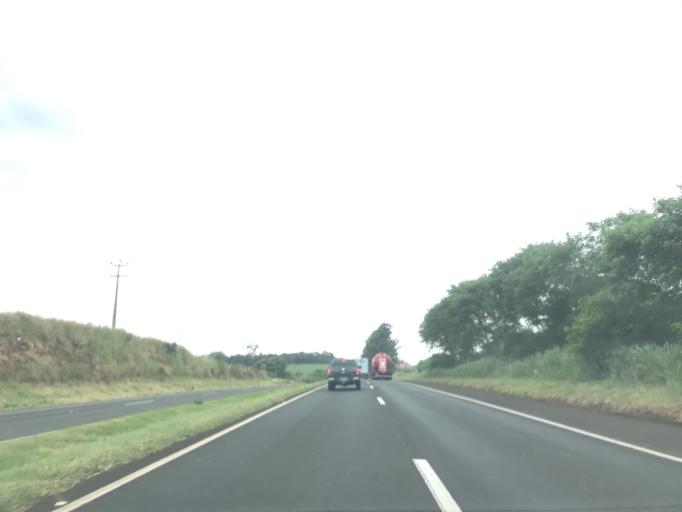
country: BR
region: Parana
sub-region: Paicandu
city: Paicandu
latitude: -23.3860
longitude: -52.0249
